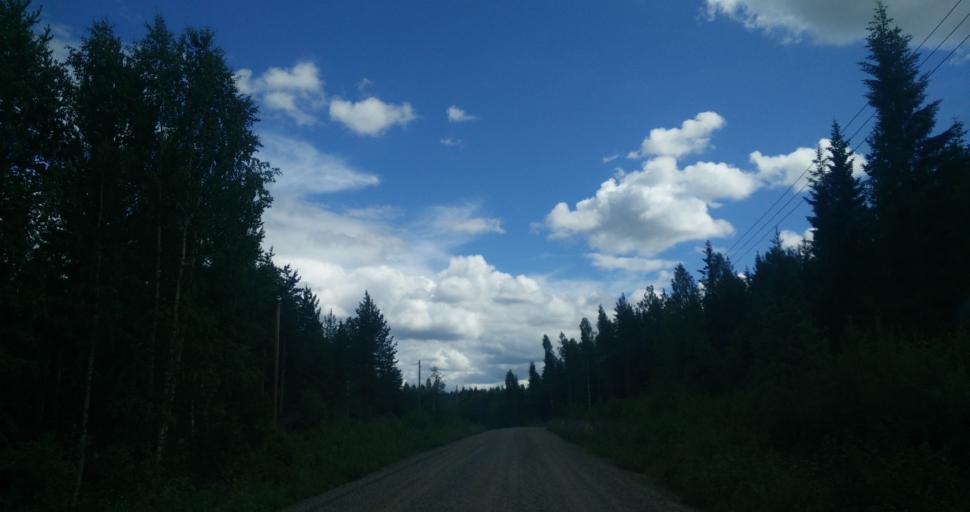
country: SE
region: Gaevleborg
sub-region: Nordanstigs Kommun
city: Bergsjoe
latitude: 62.0564
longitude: 16.8165
